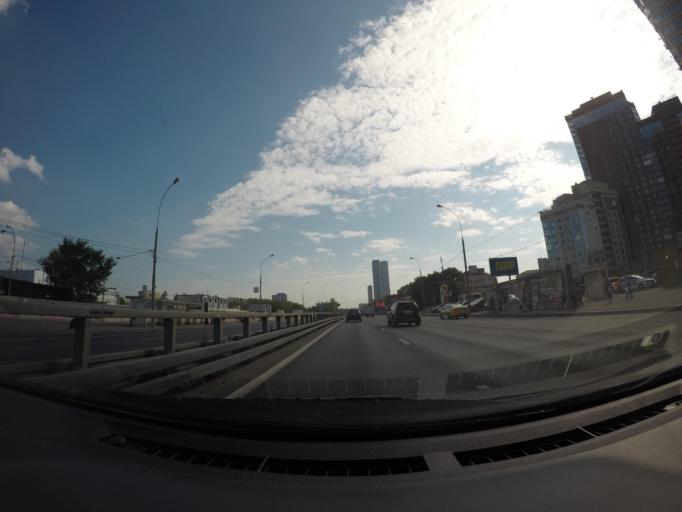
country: RU
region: Moscow
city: Likhobory
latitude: 55.8187
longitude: 37.5749
